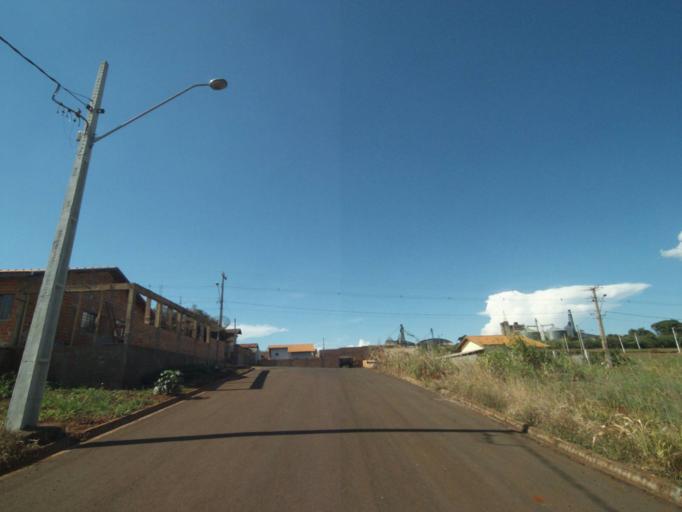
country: BR
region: Parana
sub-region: Sertanopolis
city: Sertanopolis
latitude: -23.0458
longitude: -50.8167
